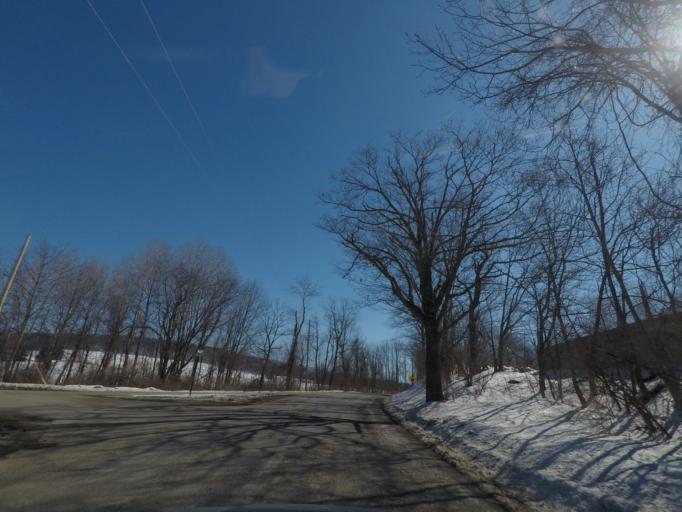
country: US
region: New York
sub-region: Saratoga County
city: Stillwater
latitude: 43.0381
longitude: -73.6844
